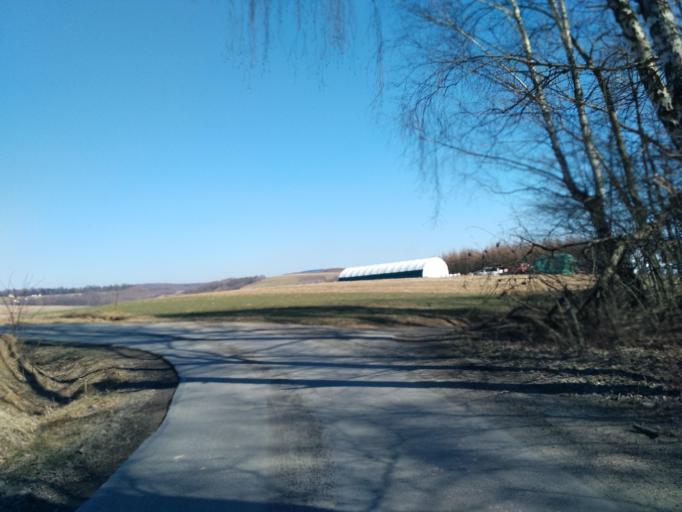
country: PL
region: Subcarpathian Voivodeship
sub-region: Powiat ropczycko-sedziszowski
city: Wielopole Skrzynskie
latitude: 49.9499
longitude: 21.5848
